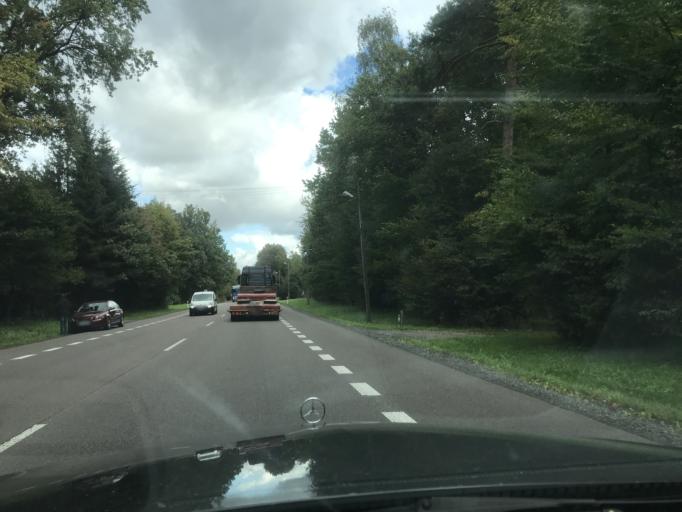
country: PL
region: Lublin Voivodeship
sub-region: Powiat krasnicki
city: Krasnik
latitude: 50.9419
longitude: 22.2698
